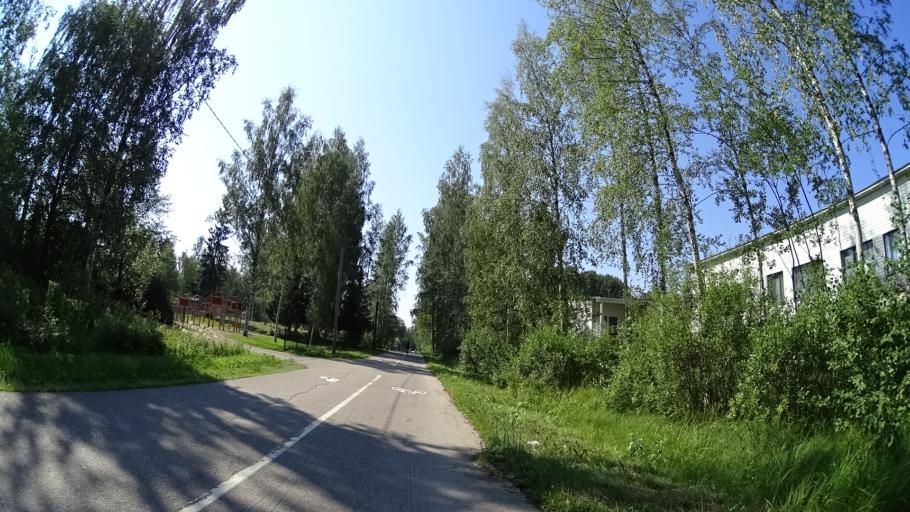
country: FI
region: Uusimaa
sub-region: Helsinki
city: Kerava
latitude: 60.3832
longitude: 25.0935
